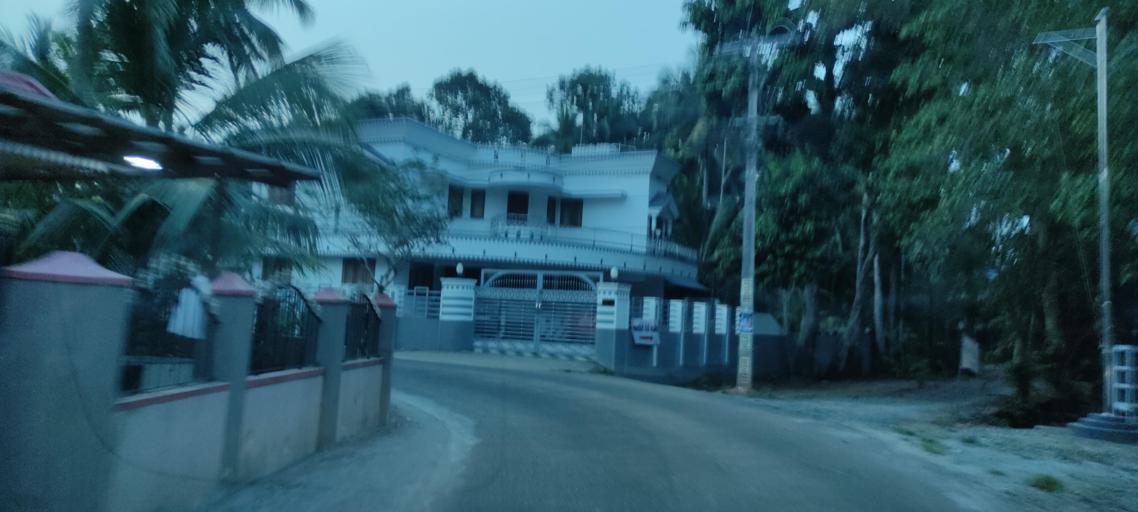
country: IN
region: Kerala
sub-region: Pattanamtitta
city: Tiruvalla
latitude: 9.3319
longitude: 76.5055
